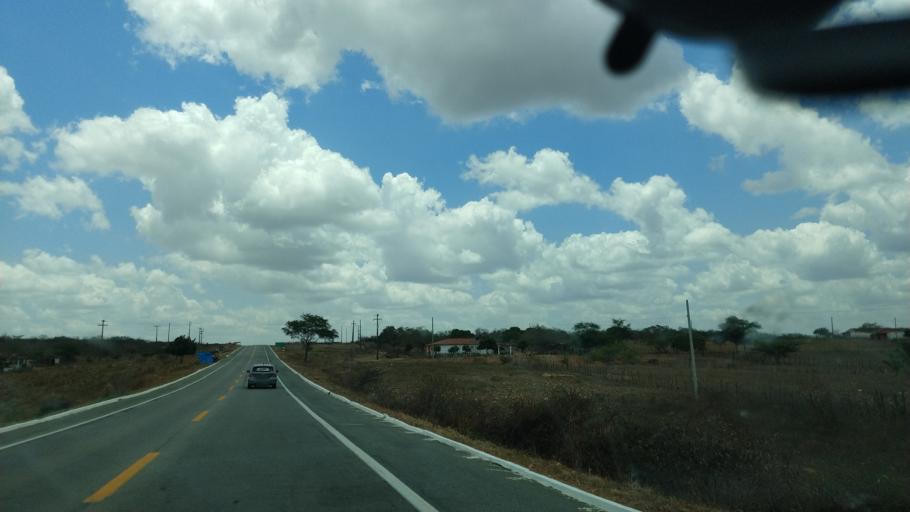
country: BR
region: Rio Grande do Norte
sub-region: Cerro Cora
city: Cerro Cora
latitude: -6.1892
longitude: -36.2300
